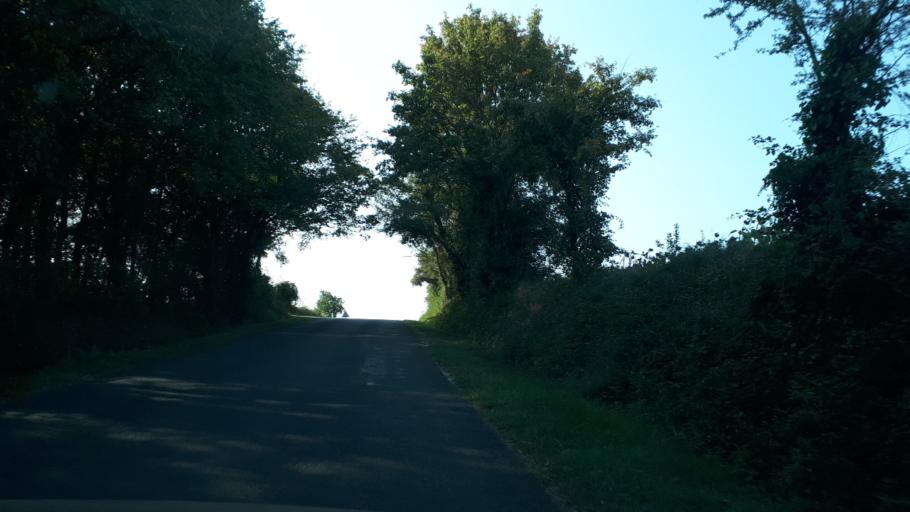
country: FR
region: Centre
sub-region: Departement du Cher
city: Rians
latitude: 47.2027
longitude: 2.5681
